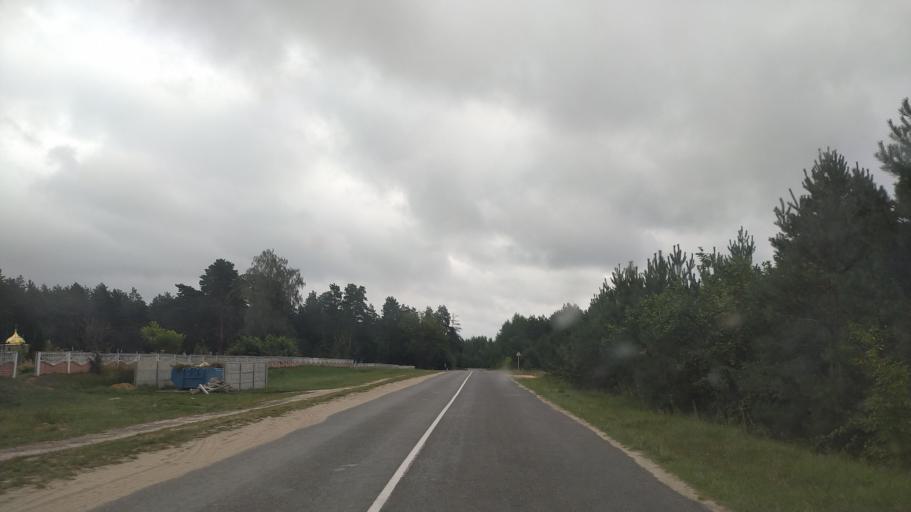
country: BY
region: Brest
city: Byaroza
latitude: 52.5981
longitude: 24.8746
